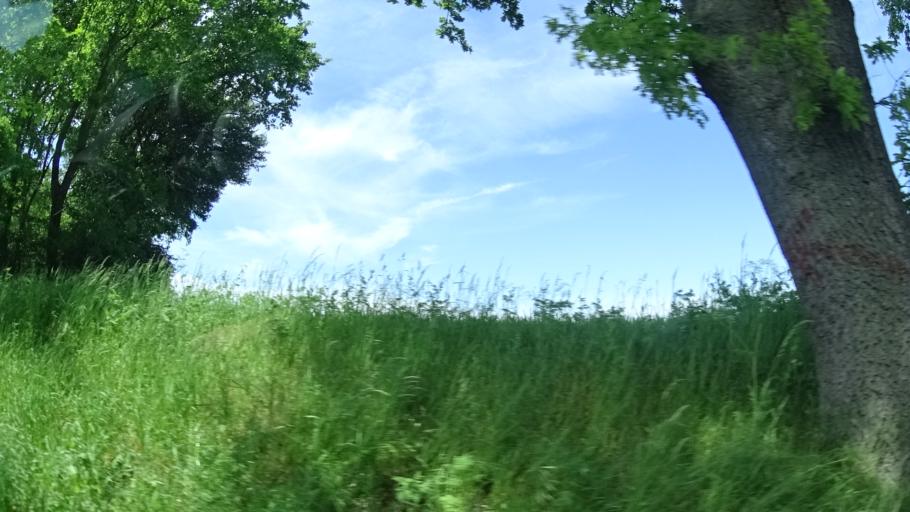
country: DE
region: Thuringia
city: Behringen
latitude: 50.7603
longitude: 10.9932
